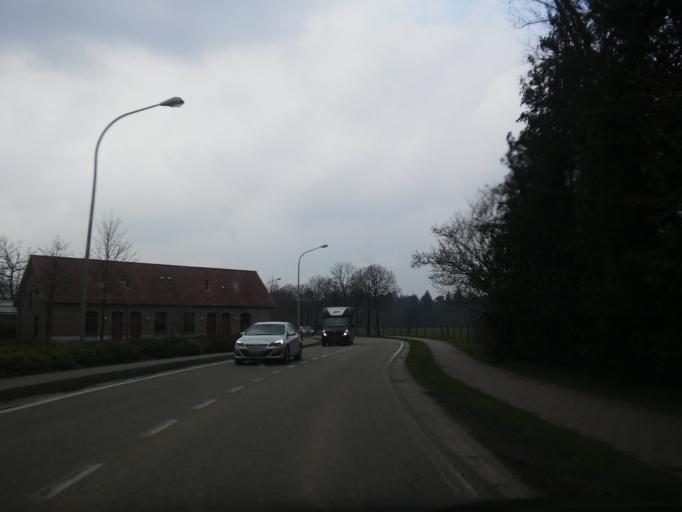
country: BE
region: Flanders
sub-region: Provincie Antwerpen
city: Grobbendonk
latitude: 51.1676
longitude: 4.7454
